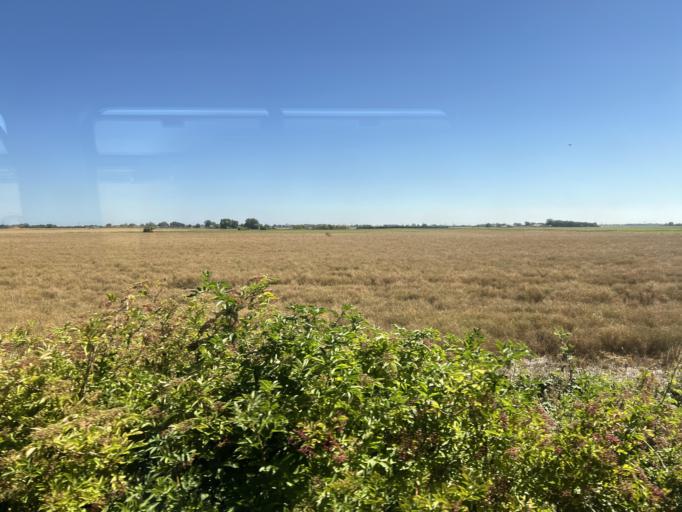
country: GB
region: England
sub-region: Lincolnshire
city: Spilsby
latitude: 53.1268
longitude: 0.1448
